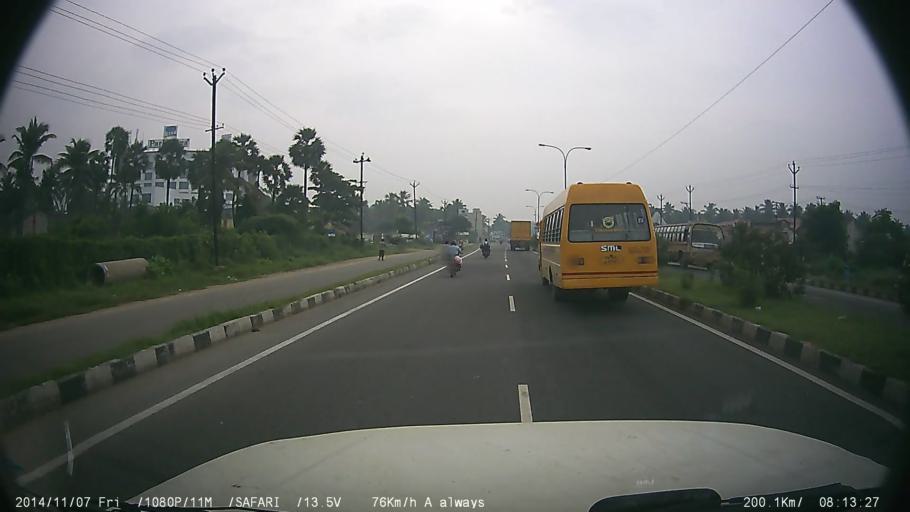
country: IN
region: Tamil Nadu
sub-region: Salem
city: Salem
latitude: 11.6925
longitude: 78.1129
